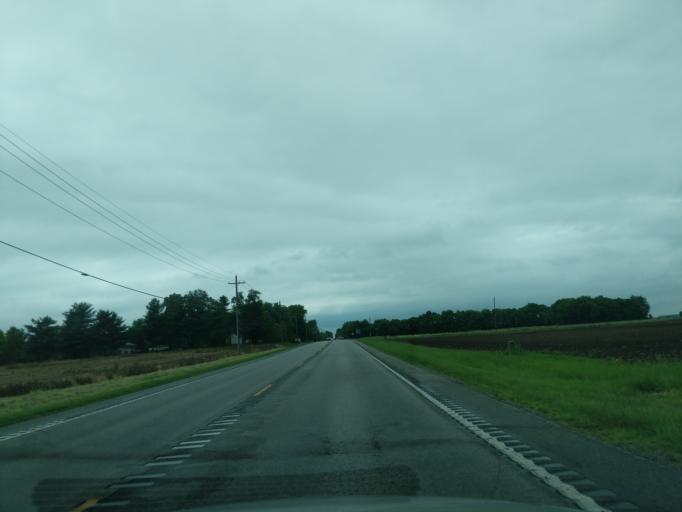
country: US
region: Indiana
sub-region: Hamilton County
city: Cicero
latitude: 40.1153
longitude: -86.0136
